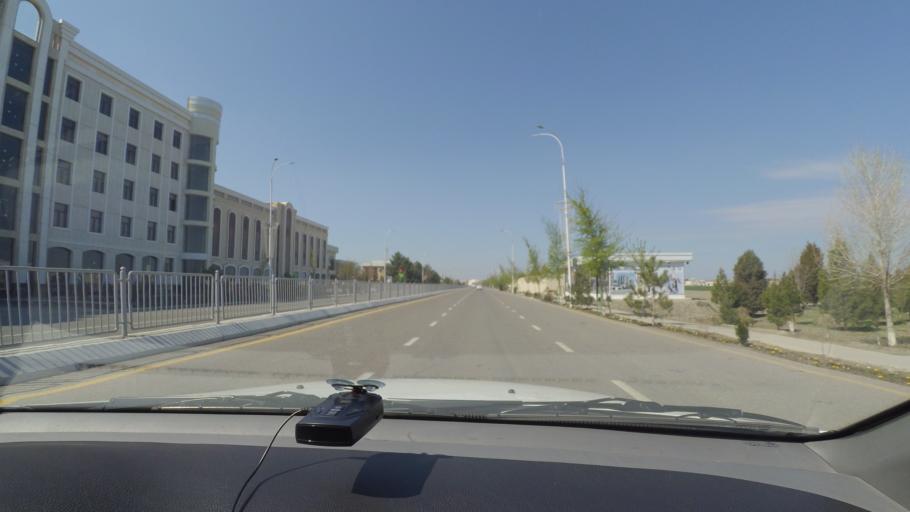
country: UZ
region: Bukhara
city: Bukhara
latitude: 39.7673
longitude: 64.4710
